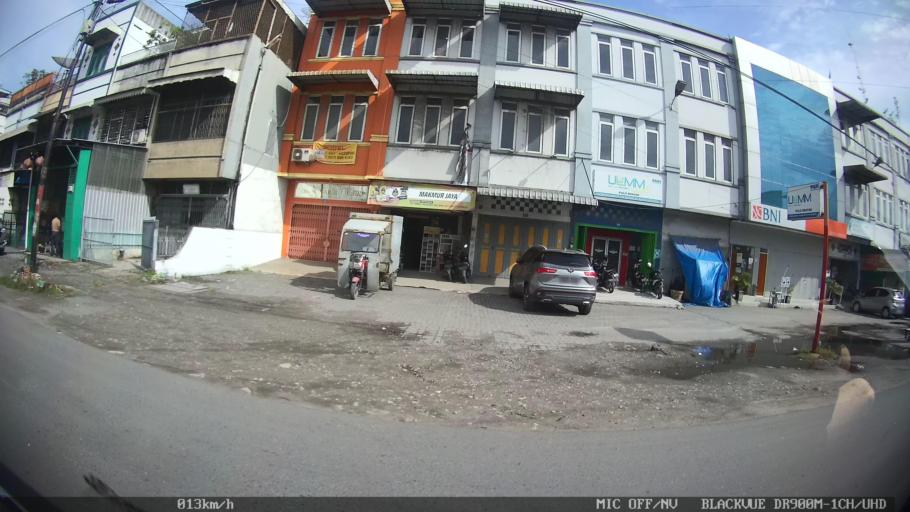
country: ID
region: North Sumatra
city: Medan
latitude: 3.6279
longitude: 98.6599
